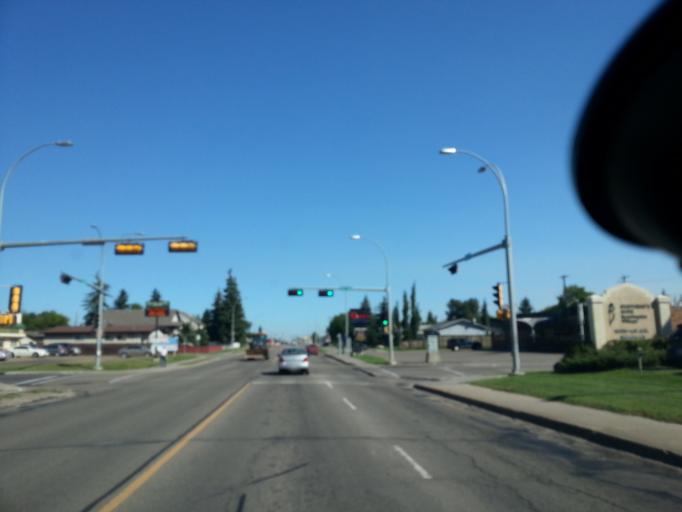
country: CA
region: Alberta
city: Edmonton
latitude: 53.5960
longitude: -113.5412
